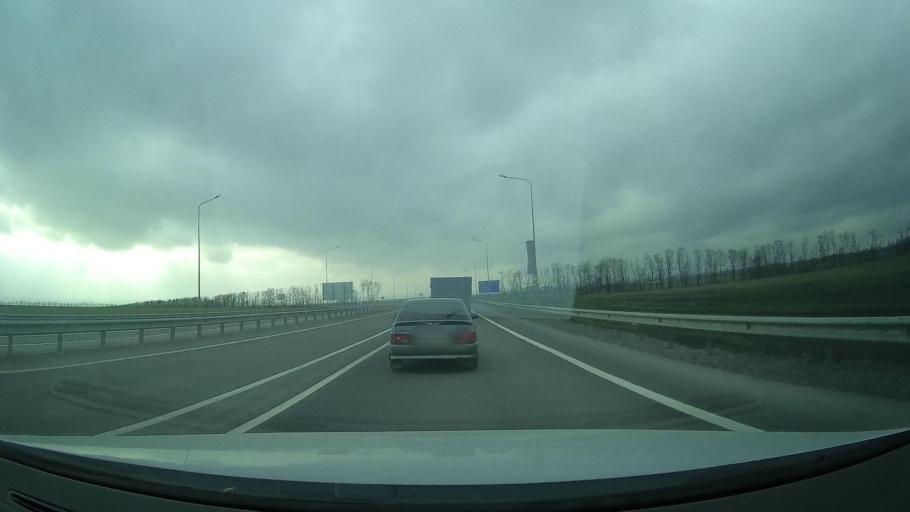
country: RU
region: Rostov
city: Grushevskaya
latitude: 47.5009
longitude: 39.9656
